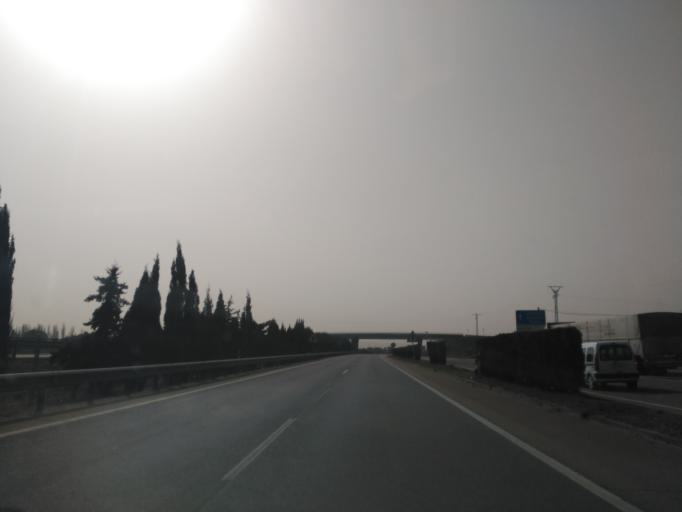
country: ES
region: Castille and Leon
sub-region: Provincia de Valladolid
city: Cubillas de Santa Marta
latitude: 41.8096
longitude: -4.5835
